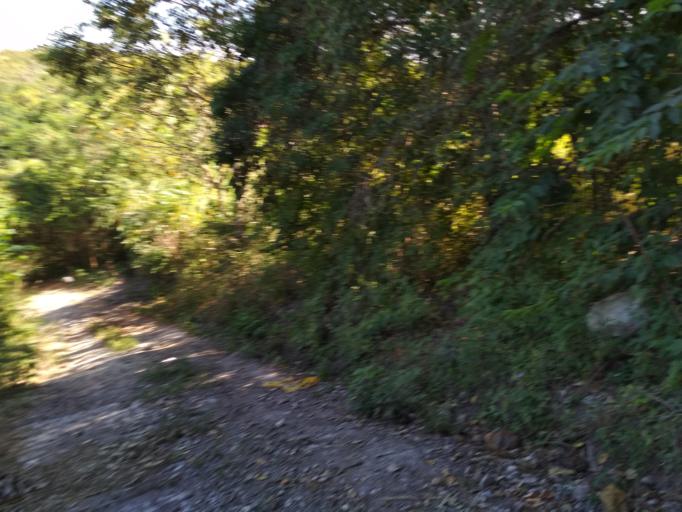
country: MX
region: Veracruz
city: Rinconada
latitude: 19.3573
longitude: -96.5582
